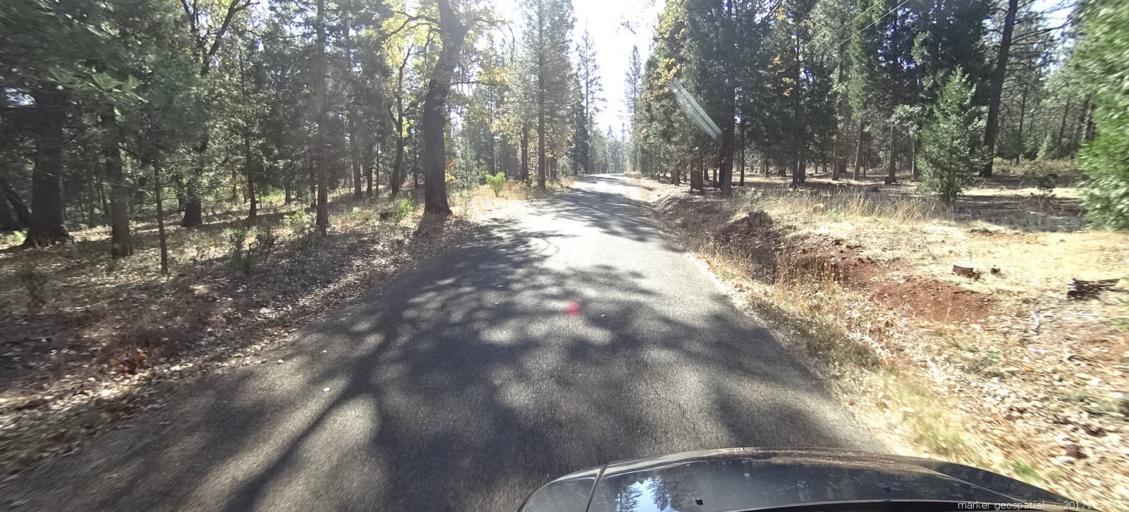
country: US
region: California
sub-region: Shasta County
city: Shingletown
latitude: 40.6282
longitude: -121.8949
